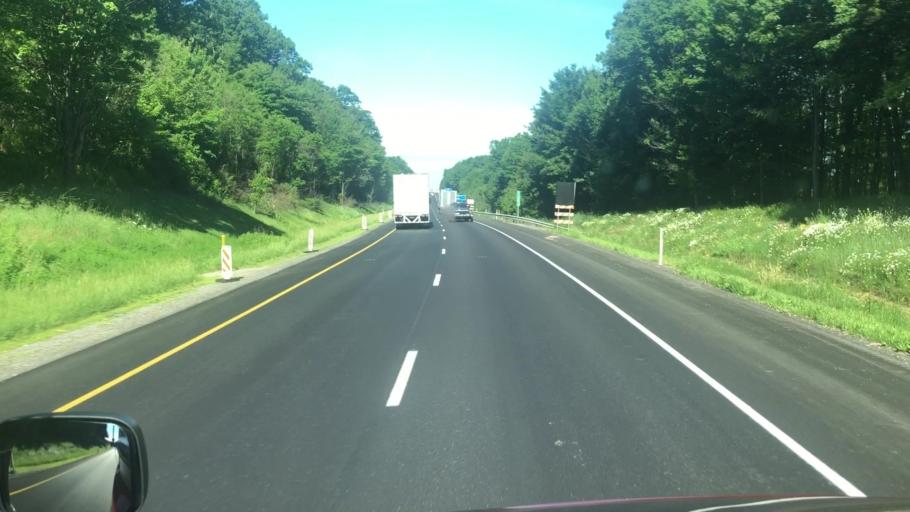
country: US
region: Pennsylvania
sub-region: Centre County
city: Milesburg
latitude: 41.0251
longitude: -77.9144
